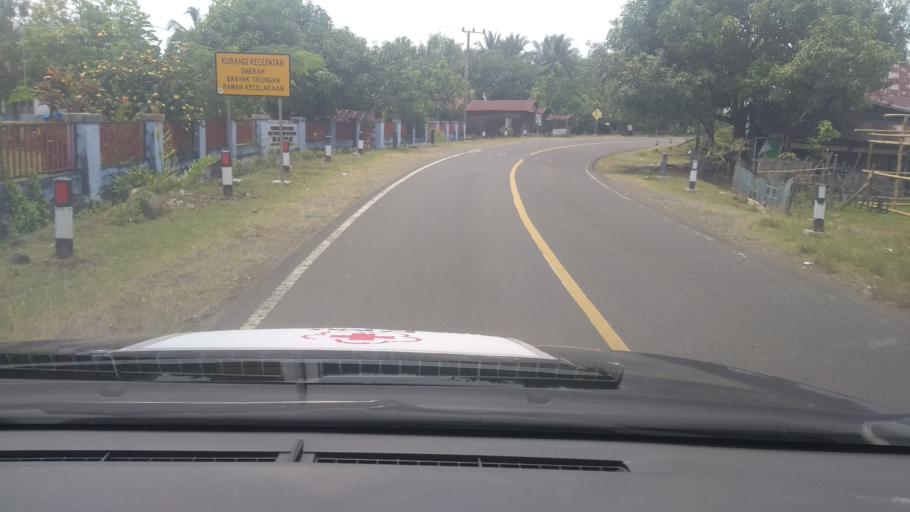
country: ID
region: Sulawesi Barat
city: Tapalang
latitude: -2.8505
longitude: 118.8553
